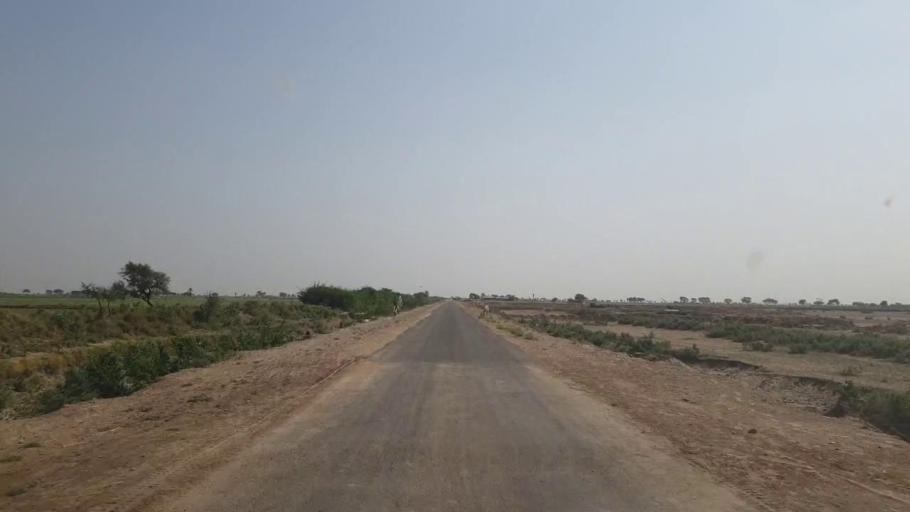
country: PK
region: Sindh
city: Jati
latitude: 24.4640
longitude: 68.5107
